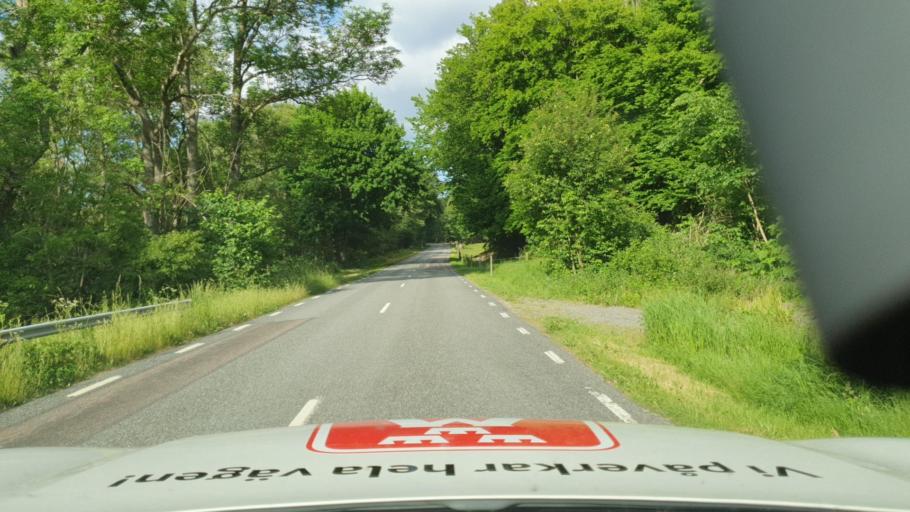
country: SE
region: Skane
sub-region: Simrishamns Kommun
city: Kivik
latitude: 55.6189
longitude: 14.2409
